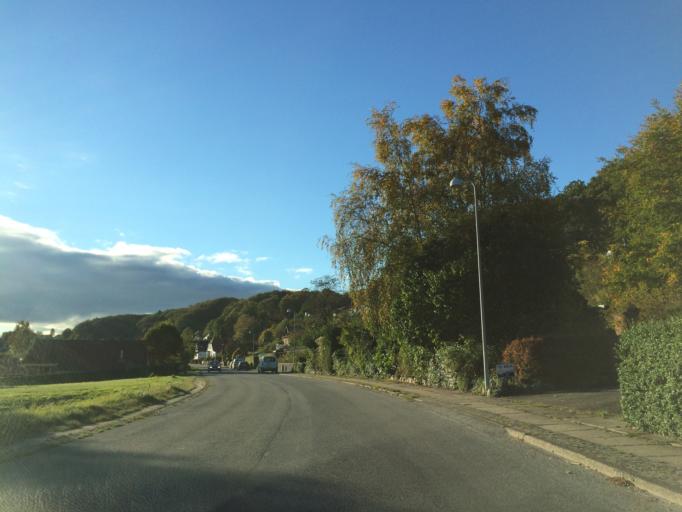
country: DK
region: Central Jutland
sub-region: Skanderborg Kommune
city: Ry
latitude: 56.1264
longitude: 9.7255
